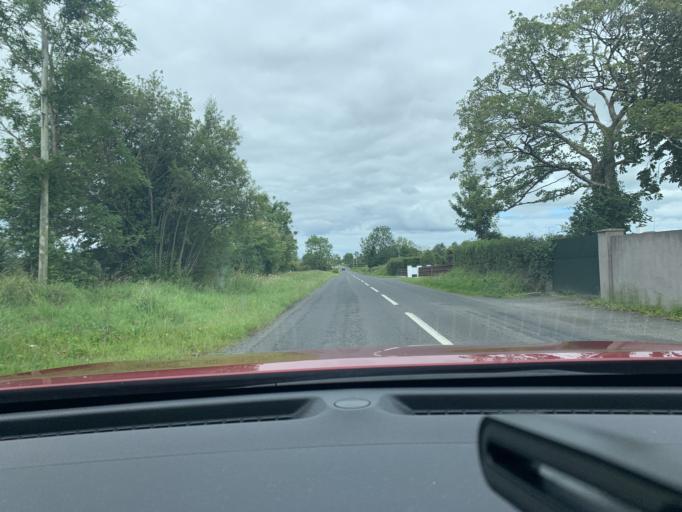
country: GB
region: Northern Ireland
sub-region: Fermanagh District
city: Enniskillen
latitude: 54.2727
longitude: -7.7040
